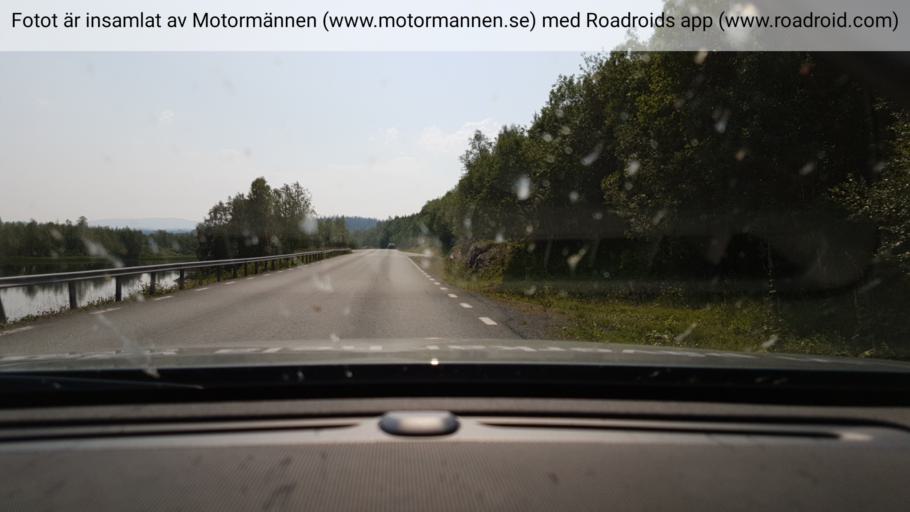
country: NO
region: Nordland
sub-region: Rana
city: Mo i Rana
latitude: 65.7297
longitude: 15.1706
